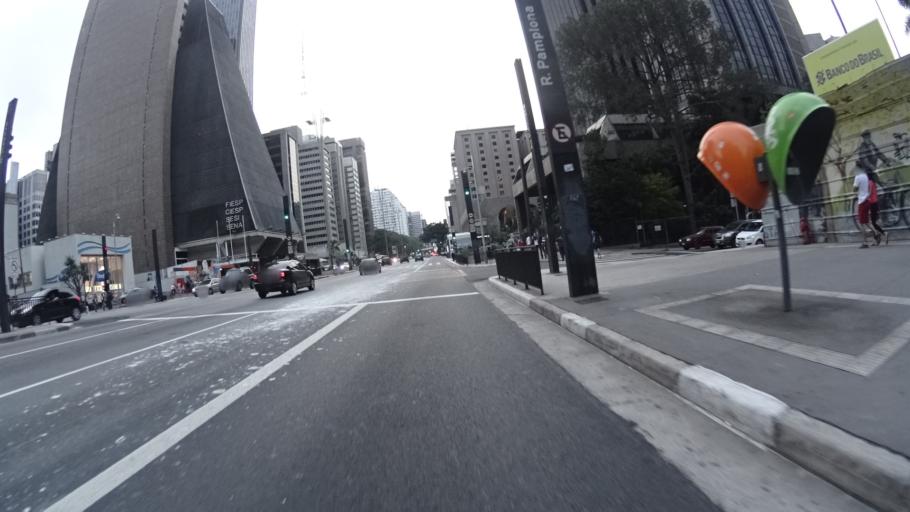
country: BR
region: Sao Paulo
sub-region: Sao Paulo
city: Sao Paulo
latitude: -23.5638
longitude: -46.6534
